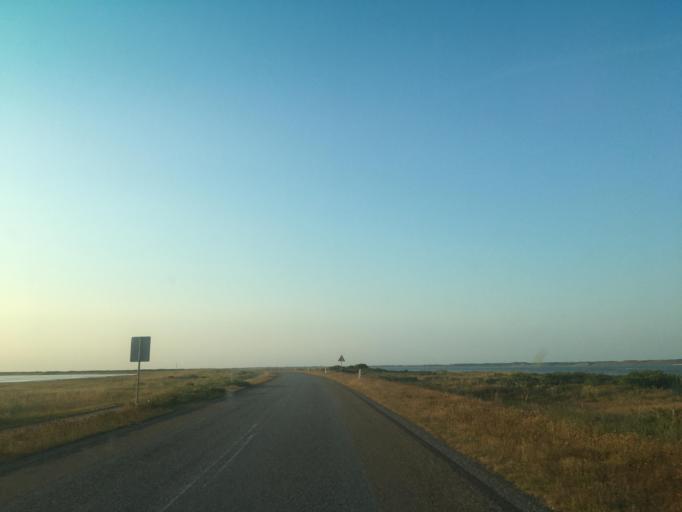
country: DK
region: Central Jutland
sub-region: Lemvig Kommune
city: Thyboron
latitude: 56.7064
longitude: 8.2471
